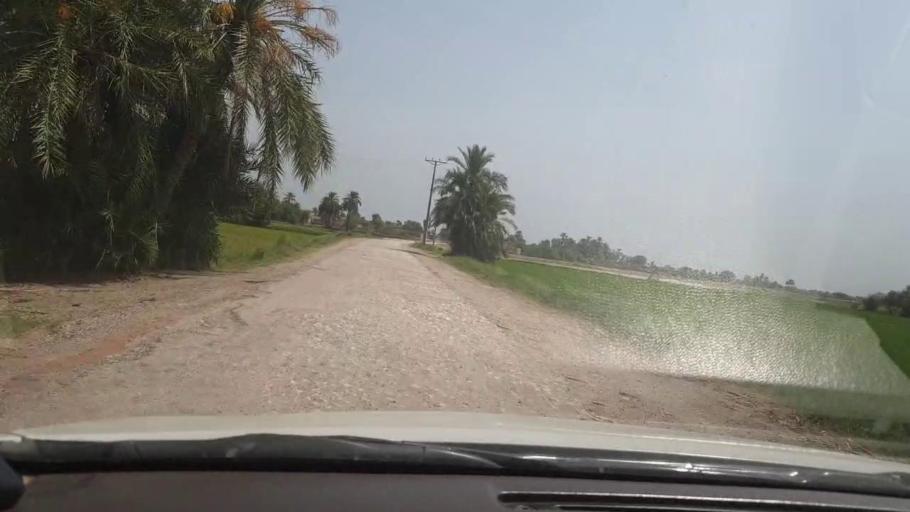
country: PK
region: Sindh
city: Shikarpur
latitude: 27.9367
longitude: 68.6000
